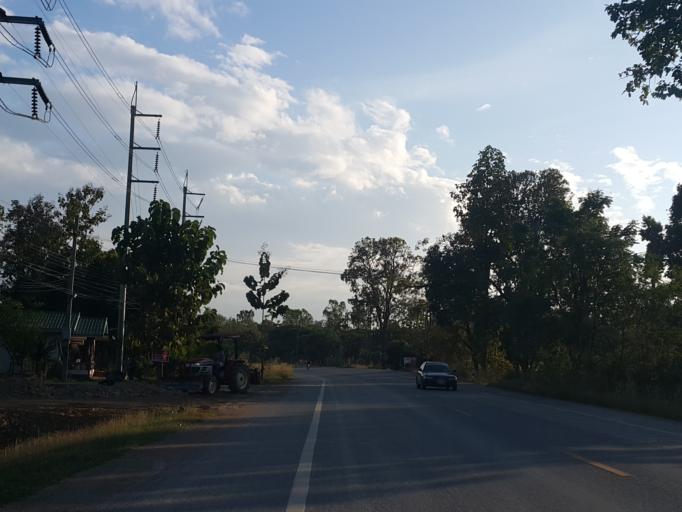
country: TH
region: Lampang
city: Lampang
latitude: 18.4469
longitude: 99.5391
